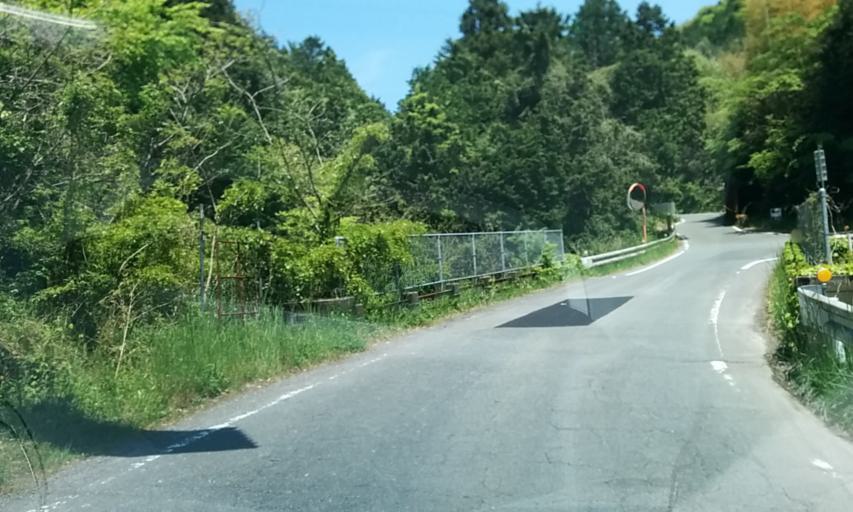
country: JP
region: Kyoto
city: Ayabe
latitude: 35.2511
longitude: 135.2746
